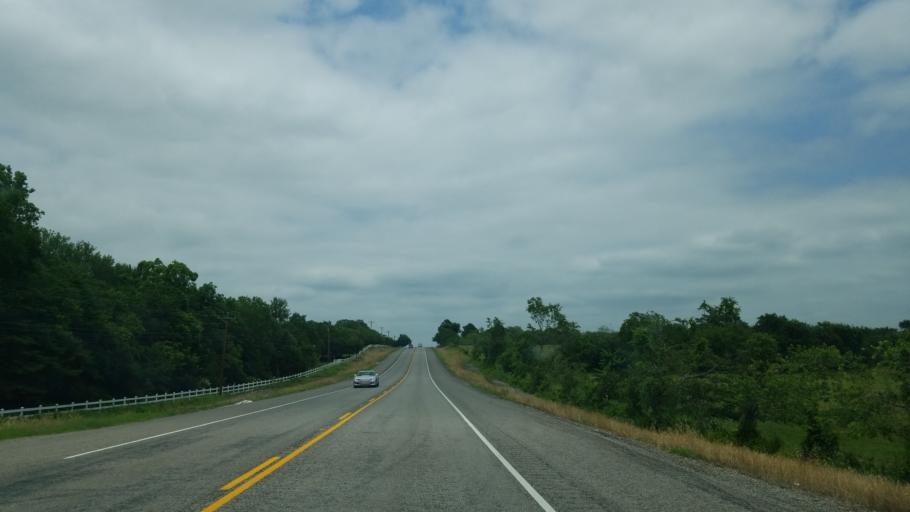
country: US
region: Texas
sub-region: Denton County
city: Denton
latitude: 33.2892
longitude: -97.0838
